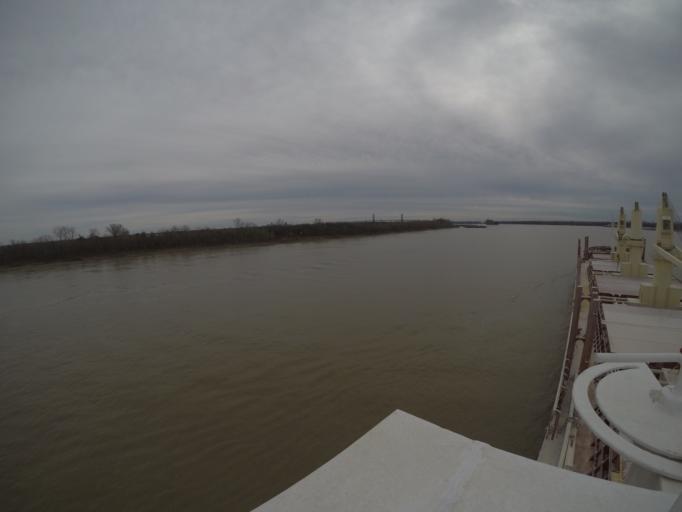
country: US
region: Louisiana
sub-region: Saint Charles Parish
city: New Sarpy
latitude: 29.9668
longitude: -90.3953
